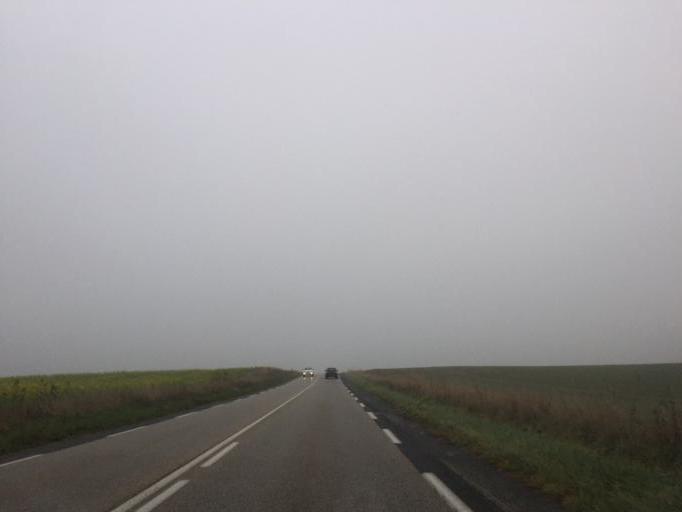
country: FR
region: Rhone-Alpes
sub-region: Departement de l'Ain
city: Mionnay
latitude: 45.9104
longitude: 4.9391
